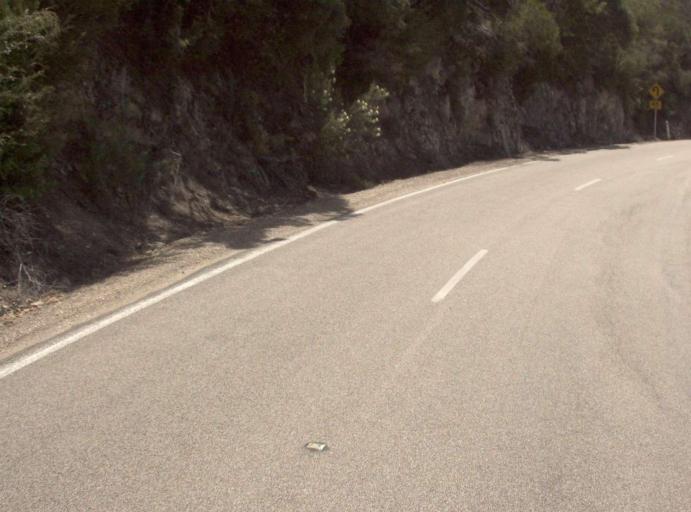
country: AU
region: Victoria
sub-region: East Gippsland
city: Lakes Entrance
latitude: -37.5571
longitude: 147.8865
